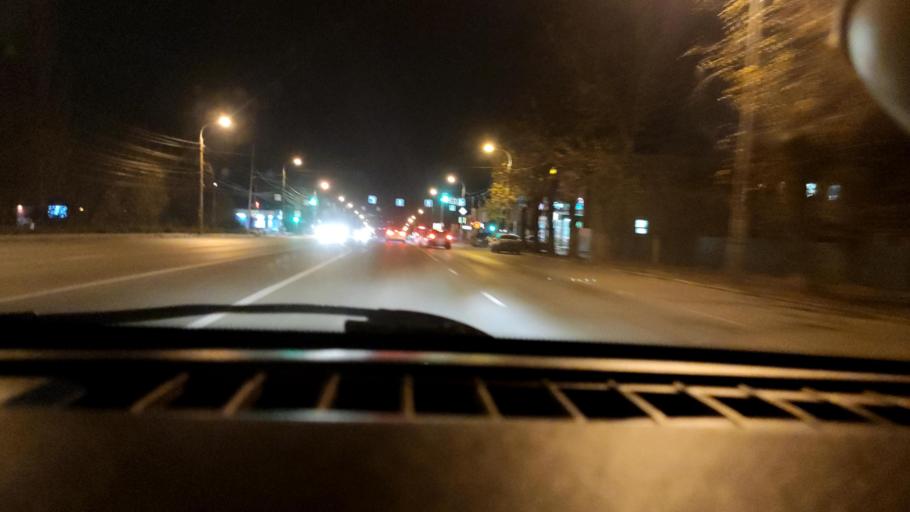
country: RU
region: Samara
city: Samara
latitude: 53.1859
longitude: 50.1913
